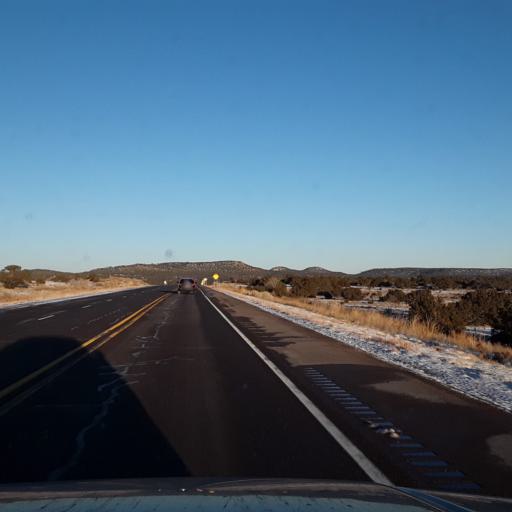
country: US
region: New Mexico
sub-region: Lincoln County
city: Carrizozo
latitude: 34.2362
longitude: -105.6129
